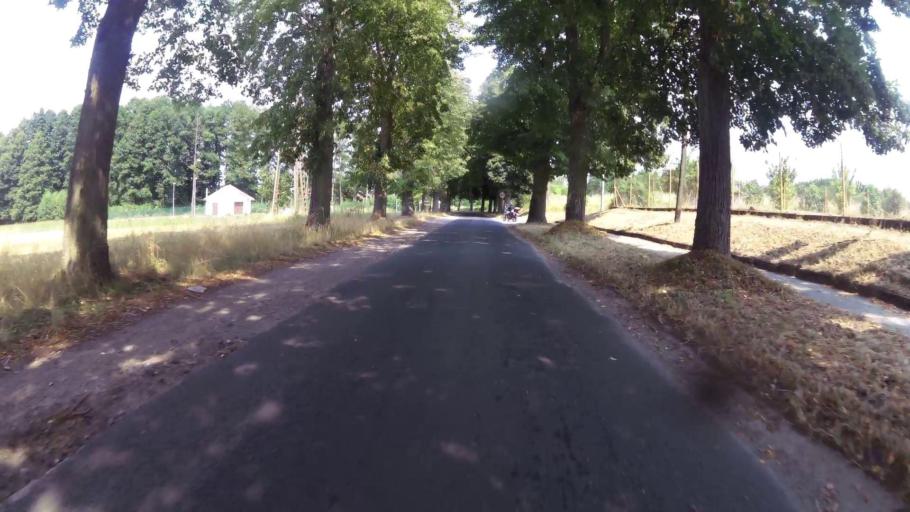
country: PL
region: West Pomeranian Voivodeship
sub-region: Powiat mysliborski
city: Mysliborz
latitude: 52.8469
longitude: 14.7787
